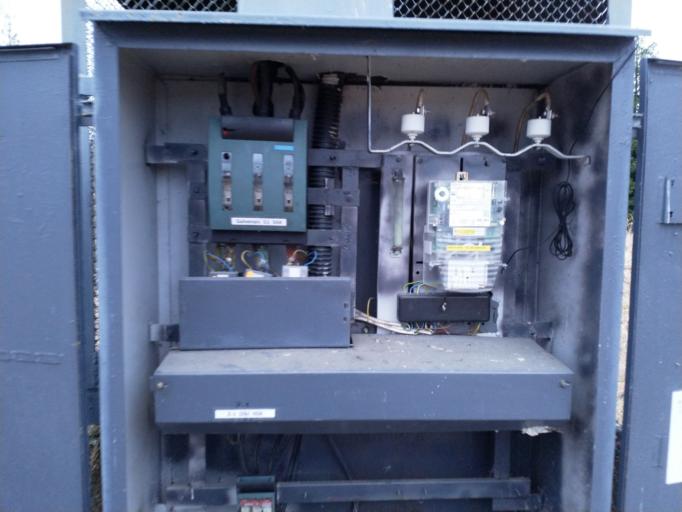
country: LV
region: Saldus Rajons
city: Saldus
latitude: 56.8941
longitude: 22.3257
